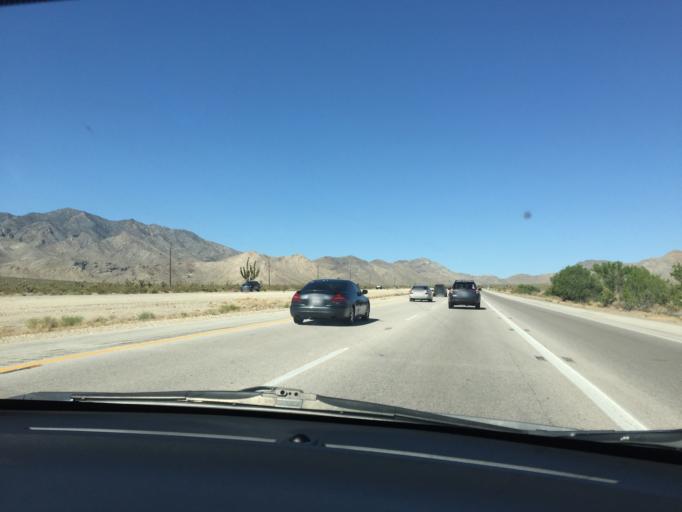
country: US
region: Nevada
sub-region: Clark County
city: Sandy Valley
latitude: 35.4581
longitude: -115.6338
